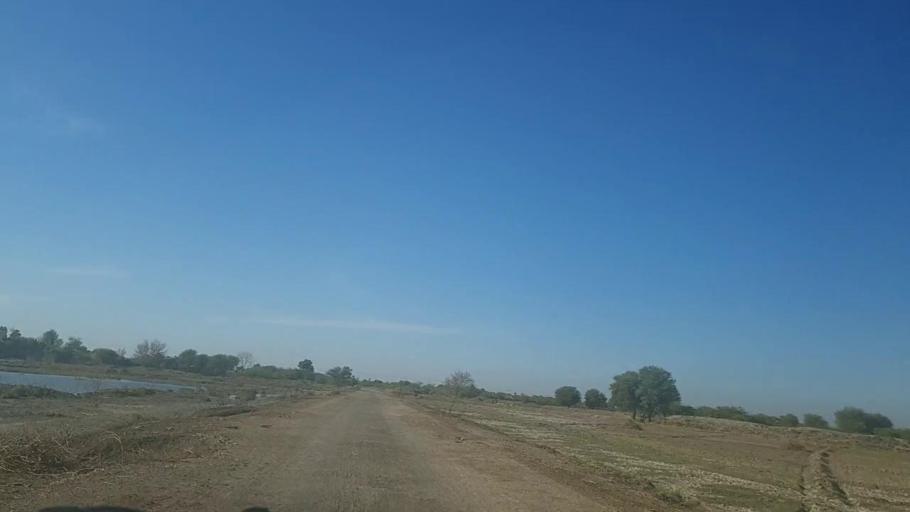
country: PK
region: Sindh
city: Pithoro
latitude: 25.5194
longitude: 69.3828
